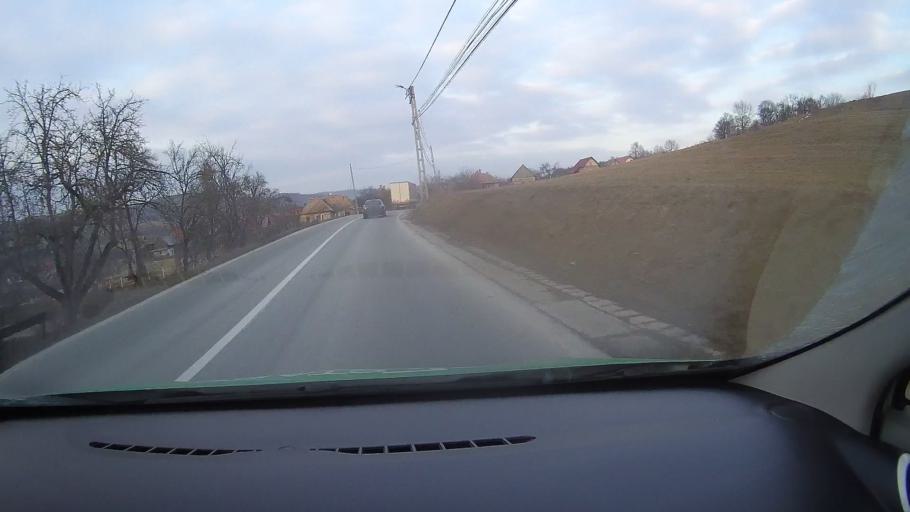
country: RO
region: Harghita
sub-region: Comuna Simonesti
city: Simonesti
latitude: 46.3391
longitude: 25.1115
